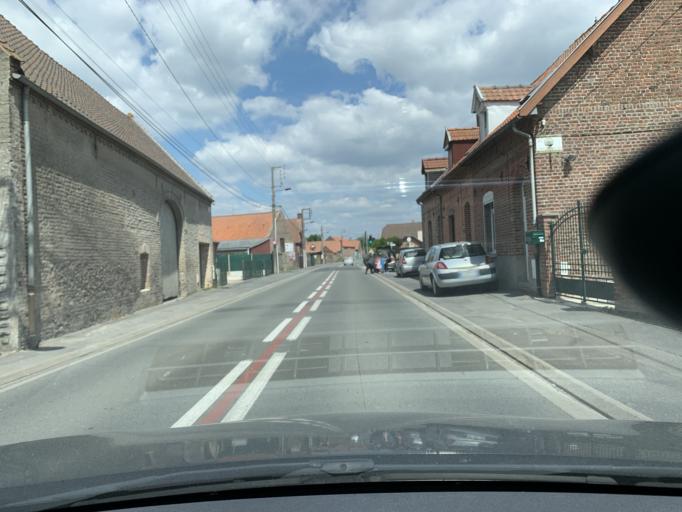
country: FR
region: Nord-Pas-de-Calais
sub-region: Departement du Nord
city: Goeulzin
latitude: 50.3154
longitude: 3.0974
